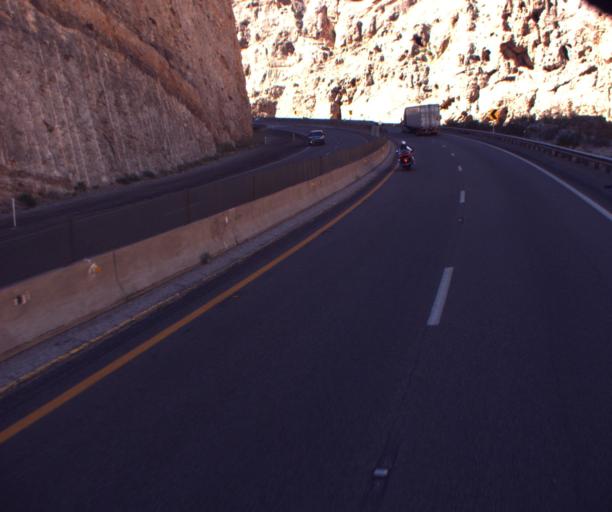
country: US
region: Arizona
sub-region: Mohave County
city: Beaver Dam
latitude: 36.9216
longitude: -113.8524
